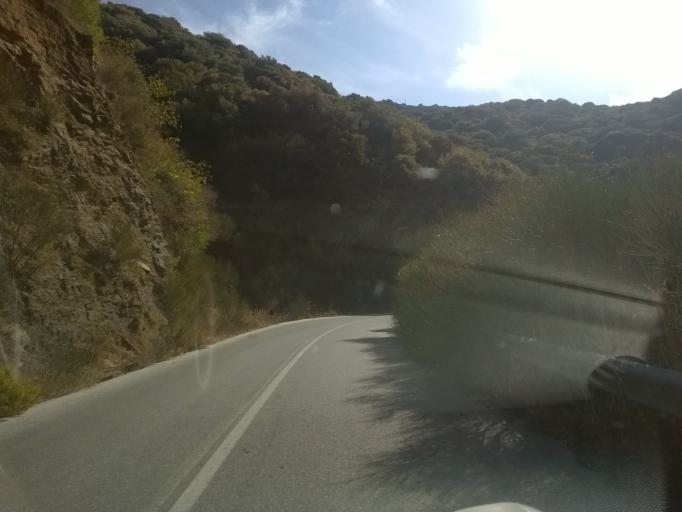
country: GR
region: South Aegean
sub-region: Nomos Kykladon
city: Filotion
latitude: 37.1410
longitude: 25.5394
